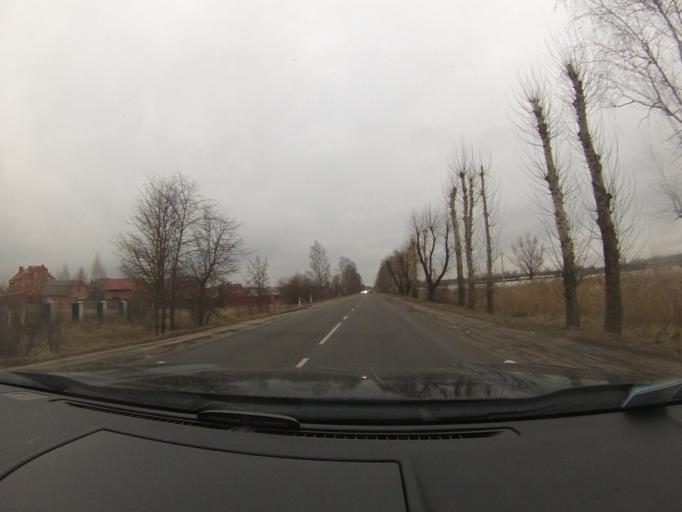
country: RU
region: Moskovskaya
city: Lopatinskiy
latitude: 55.3294
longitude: 38.7222
